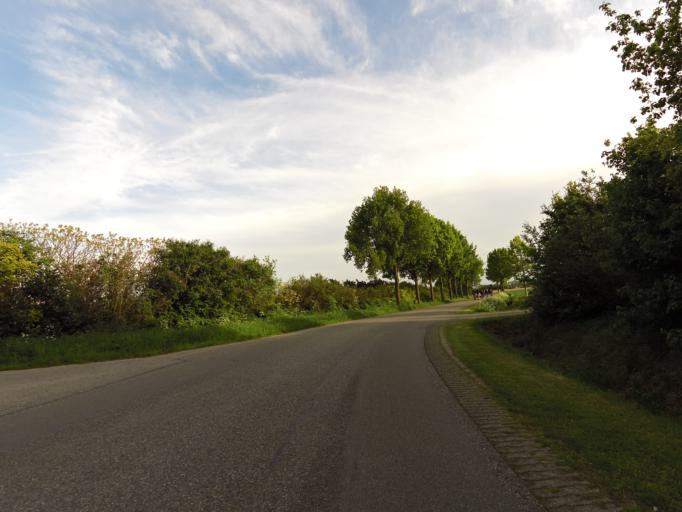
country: NL
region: Gelderland
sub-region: Gemeente Montferland
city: s-Heerenberg
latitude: 51.8987
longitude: 6.3048
